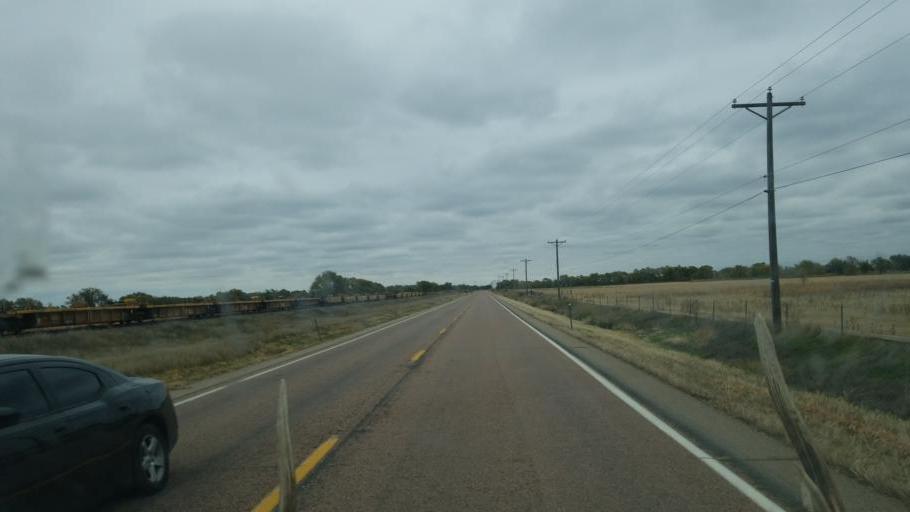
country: US
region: Colorado
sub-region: Crowley County
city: Ordway
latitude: 38.1881
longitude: -103.8698
